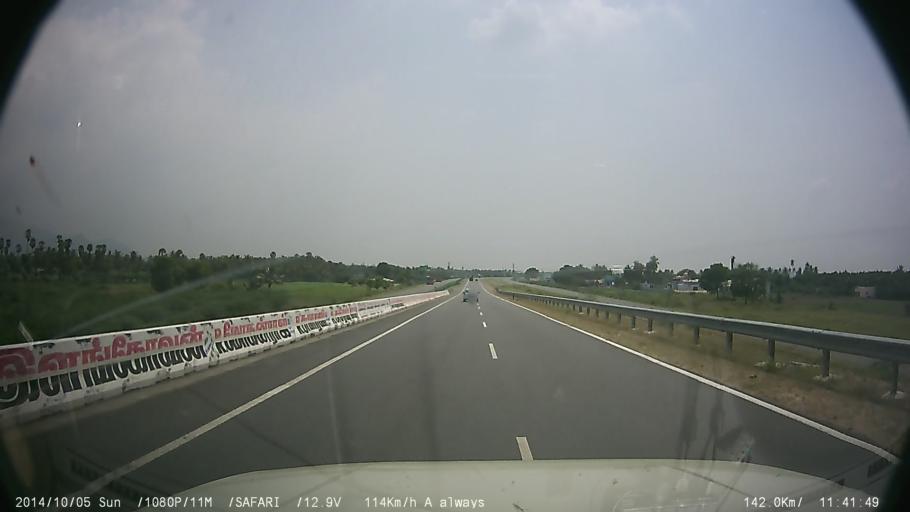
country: IN
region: Tamil Nadu
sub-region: Salem
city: Attur
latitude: 11.6073
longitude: 78.6048
